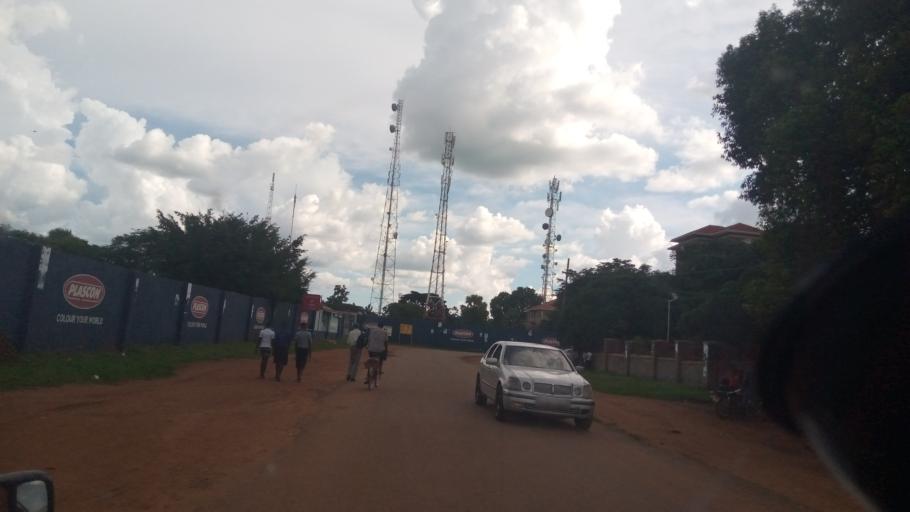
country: UG
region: Northern Region
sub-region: Lira District
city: Lira
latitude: 2.2392
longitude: 32.8956
